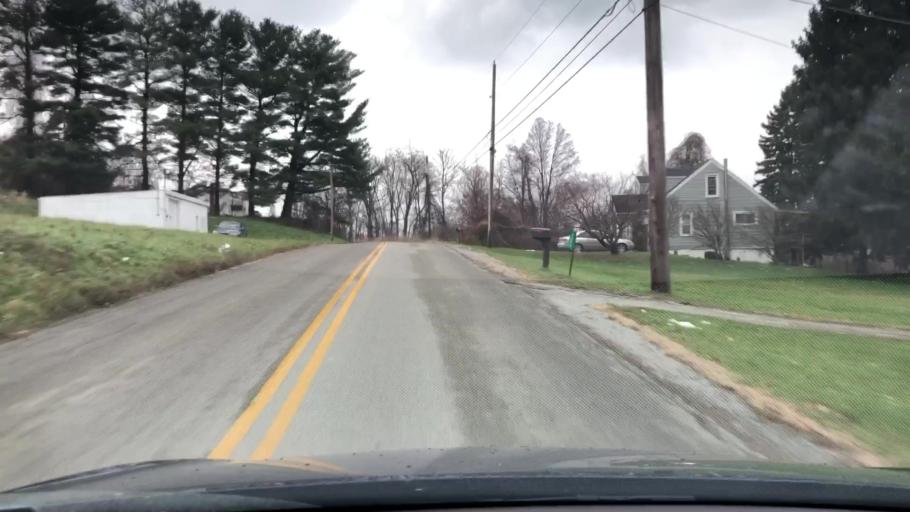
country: US
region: Pennsylvania
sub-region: Fayette County
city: Dunbar
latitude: 39.9815
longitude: -79.6271
